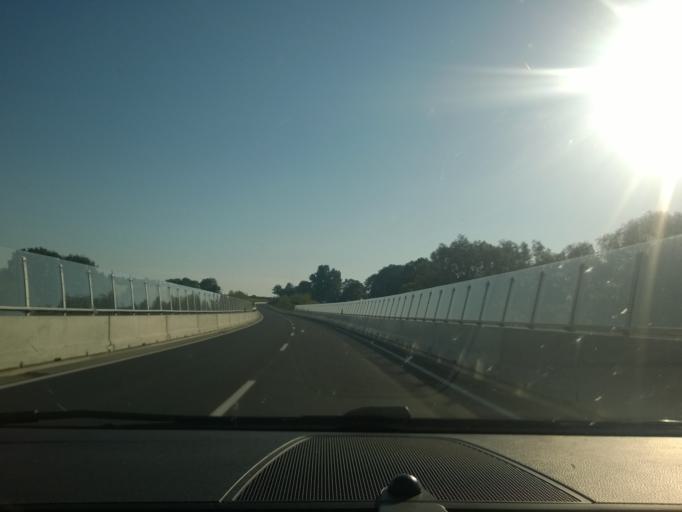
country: DE
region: North Rhine-Westphalia
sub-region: Regierungsbezirk Munster
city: Nottuln
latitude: 51.9341
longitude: 7.3467
